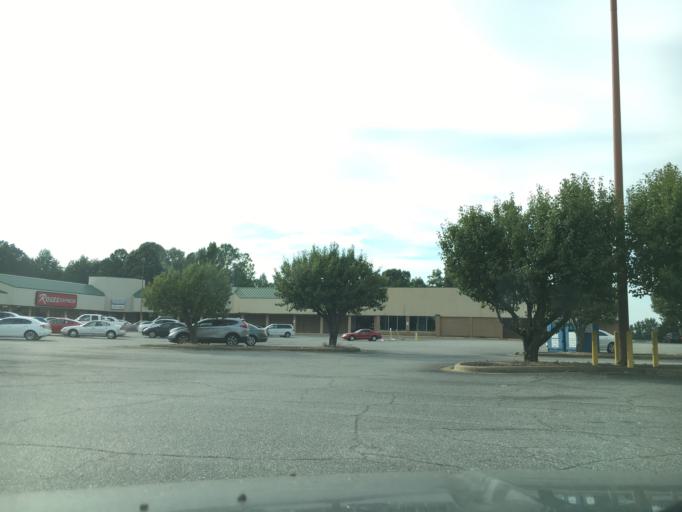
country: US
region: Virginia
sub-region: Halifax County
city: Halifax
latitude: 36.7352
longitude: -78.9195
